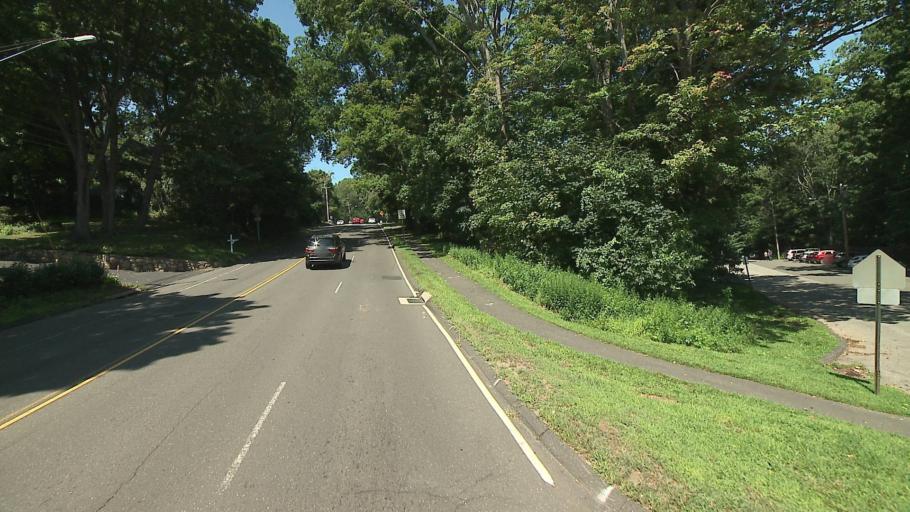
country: US
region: Connecticut
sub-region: Fairfield County
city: Trumbull
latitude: 41.2465
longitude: -73.1999
